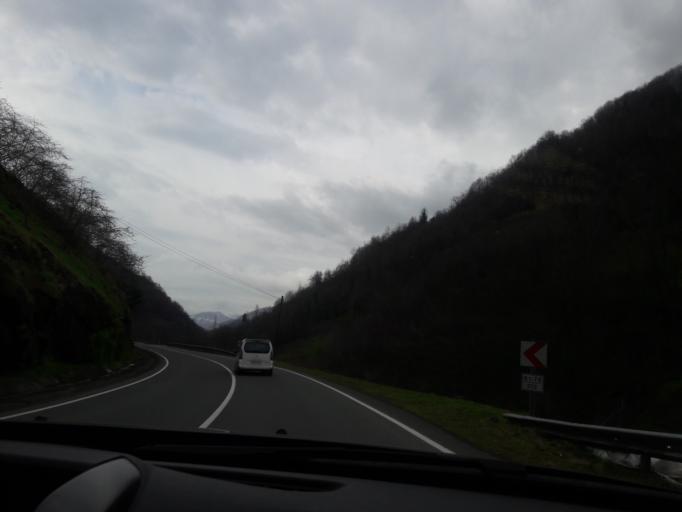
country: TR
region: Trabzon
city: Salpazari
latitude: 40.9756
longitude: 39.1976
